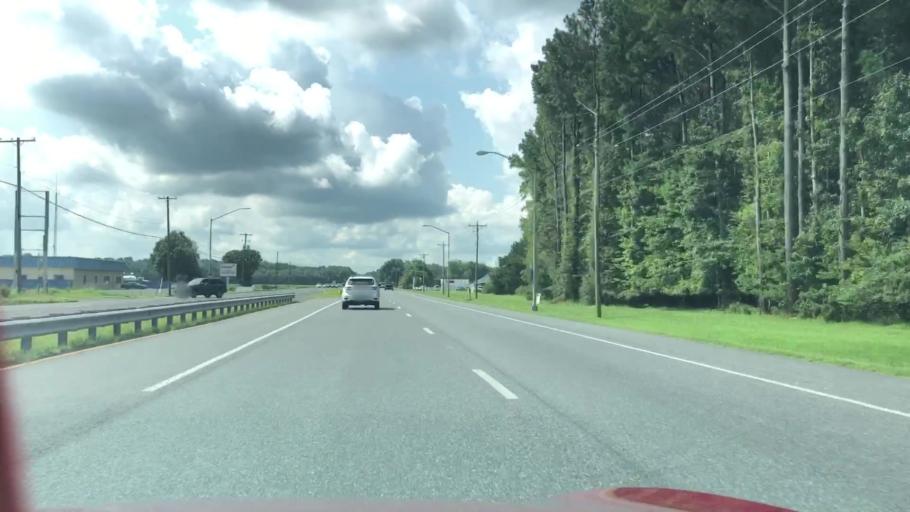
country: US
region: Maryland
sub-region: Worcester County
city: Pocomoke City
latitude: 38.0212
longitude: -75.5433
